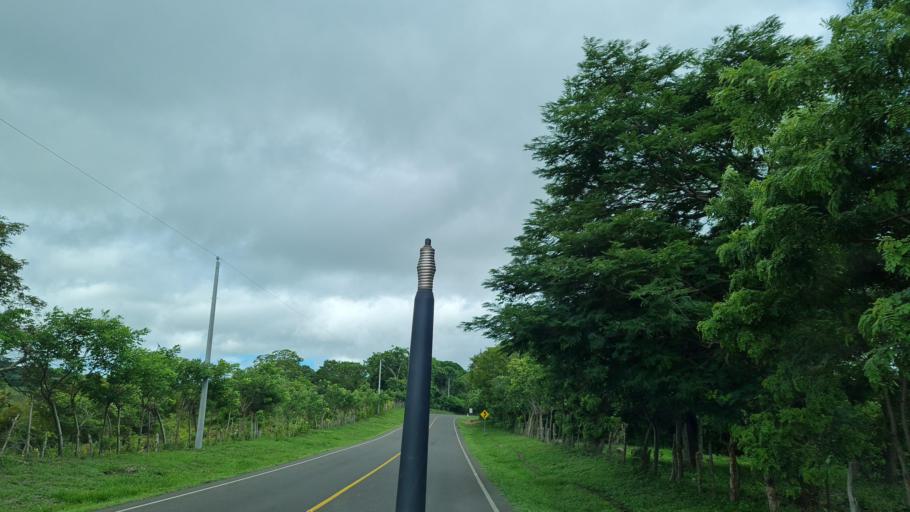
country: NI
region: Boaco
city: San Jose de los Remates
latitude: 12.5970
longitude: -85.8988
